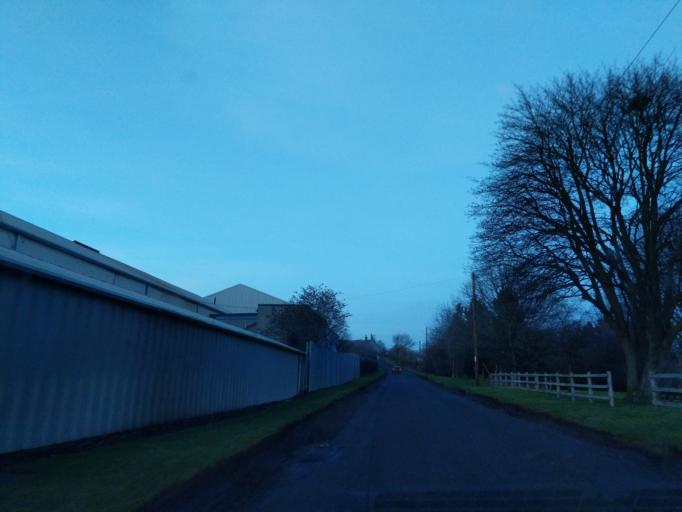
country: GB
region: Scotland
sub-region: Midlothian
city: Loanhead
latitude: 55.8819
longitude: -3.1432
